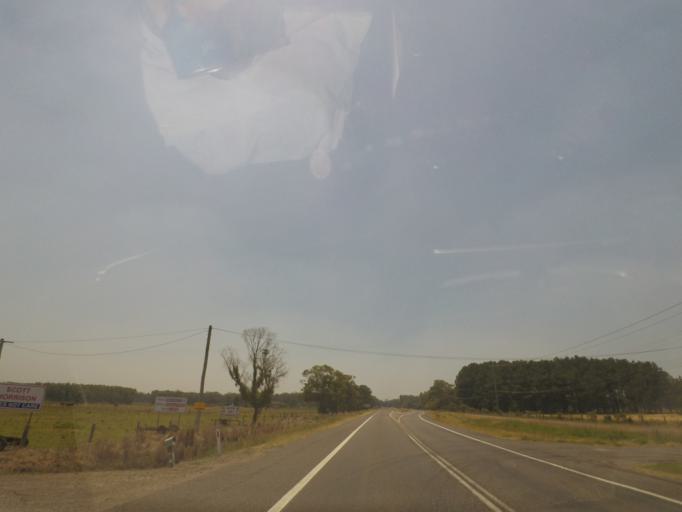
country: AU
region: New South Wales
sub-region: Port Stephens Shire
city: Medowie
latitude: -32.7944
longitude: 151.8950
